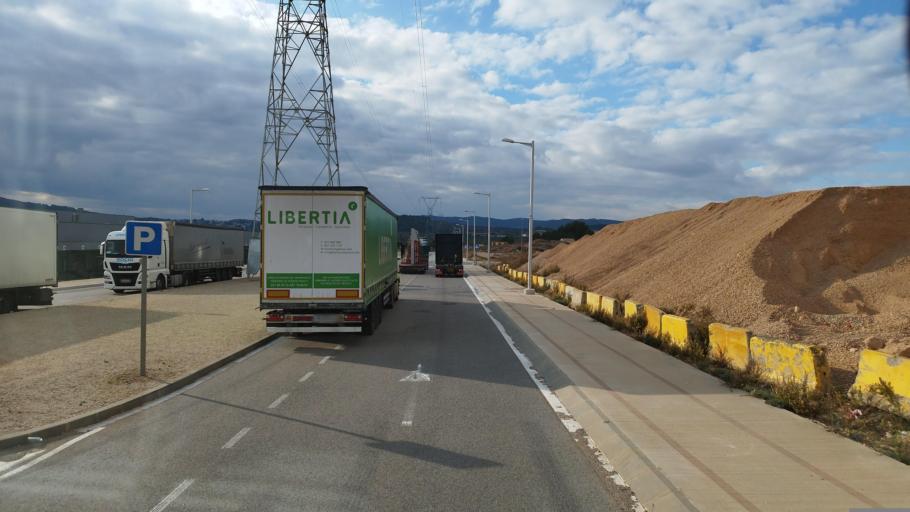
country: ES
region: Catalonia
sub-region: Provincia de Tarragona
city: la Bisbal del Penedes
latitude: 41.2759
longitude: 1.5069
